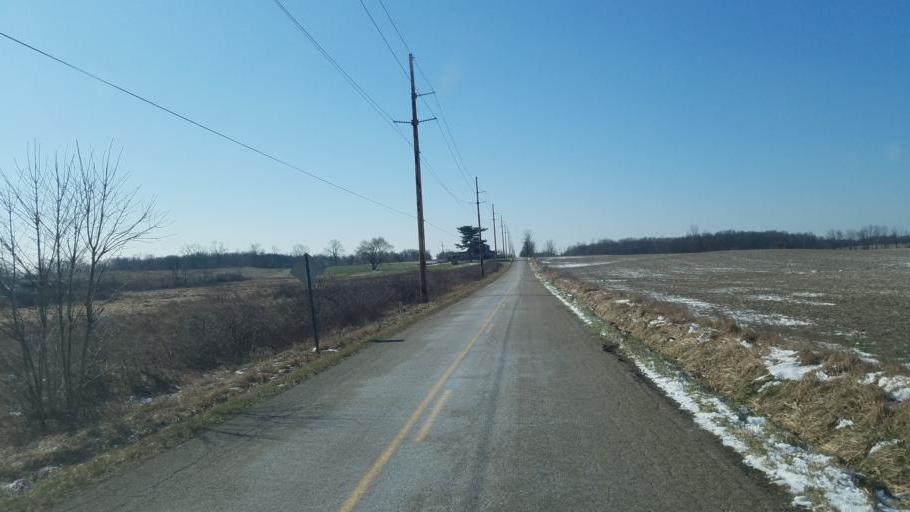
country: US
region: Ohio
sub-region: Knox County
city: Mount Vernon
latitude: 40.3179
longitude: -82.4724
